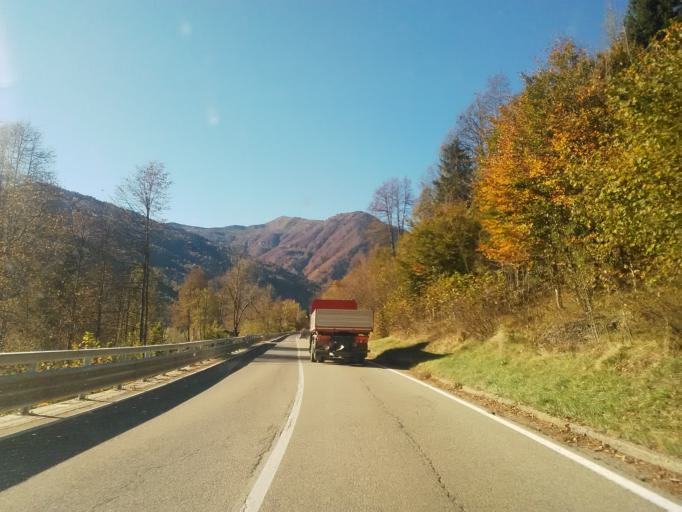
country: IT
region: Piedmont
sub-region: Provincia di Vercelli
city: Scopello
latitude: 45.7807
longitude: 8.1036
